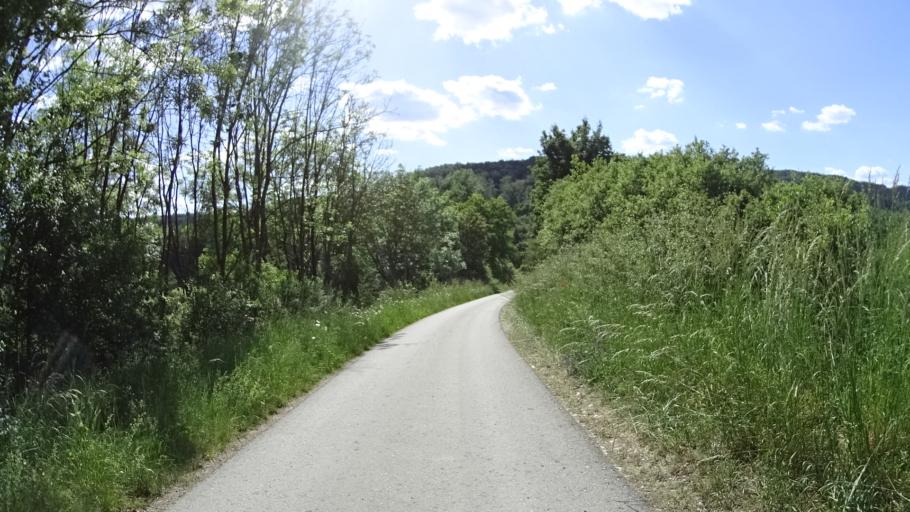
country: DE
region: Bavaria
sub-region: Regierungsbezirk Mittelfranken
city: Greding
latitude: 49.0176
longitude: 11.3598
